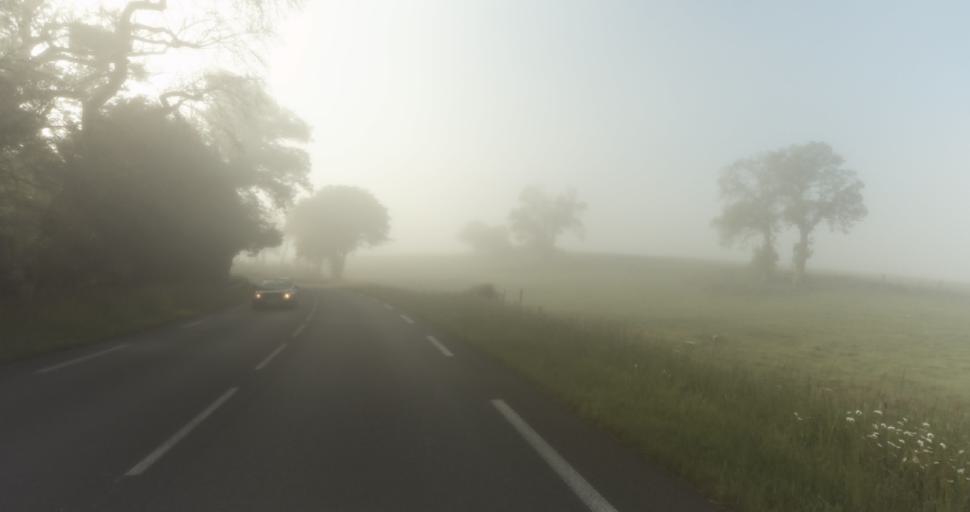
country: FR
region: Limousin
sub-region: Departement de la Haute-Vienne
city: Le Vigen
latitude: 45.7669
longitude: 1.2919
